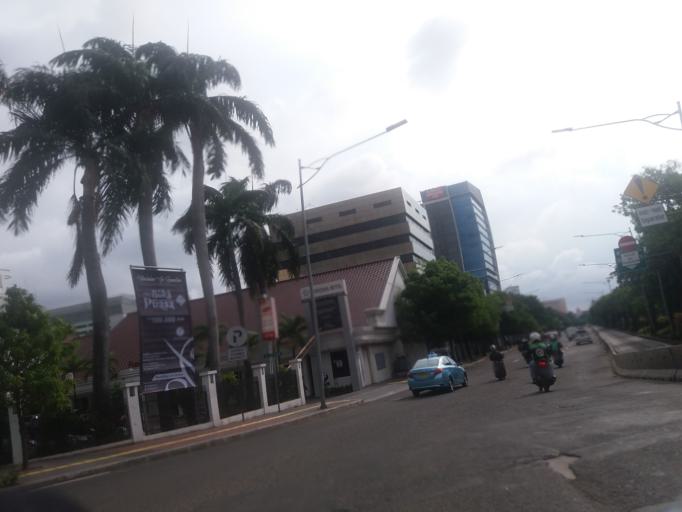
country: ID
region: Jakarta Raya
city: Jakarta
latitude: -6.1683
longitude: 106.8302
